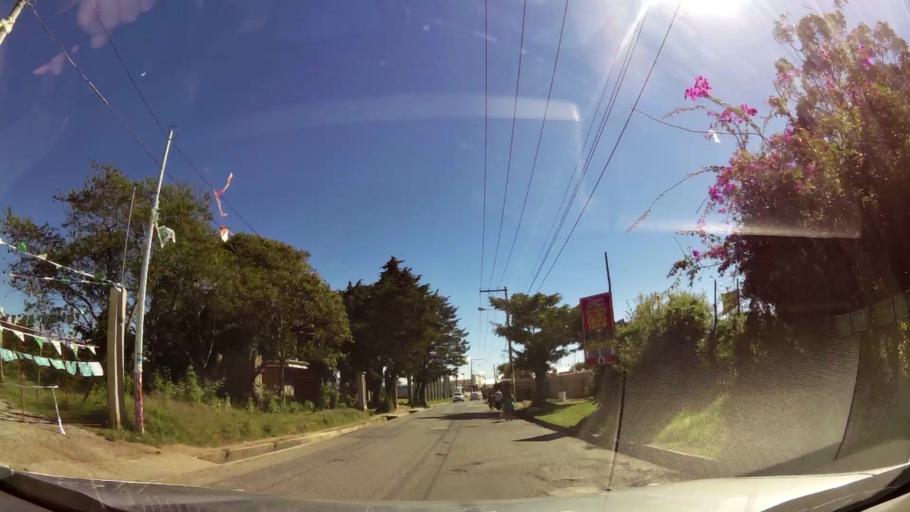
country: GT
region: Guatemala
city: San Jose Pinula
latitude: 14.5143
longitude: -90.4280
